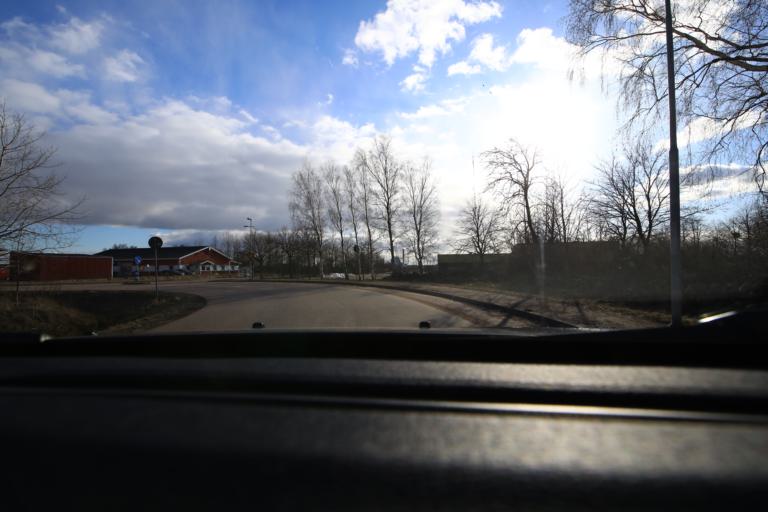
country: SE
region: Halland
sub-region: Kungsbacka Kommun
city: Frillesas
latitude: 57.2405
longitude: 12.1880
